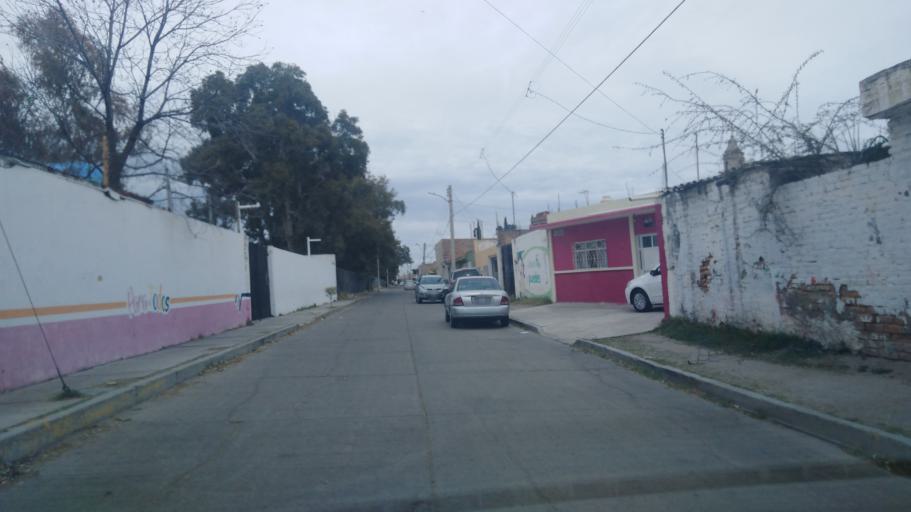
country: MX
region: Durango
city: Victoria de Durango
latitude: 24.0285
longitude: -104.6293
